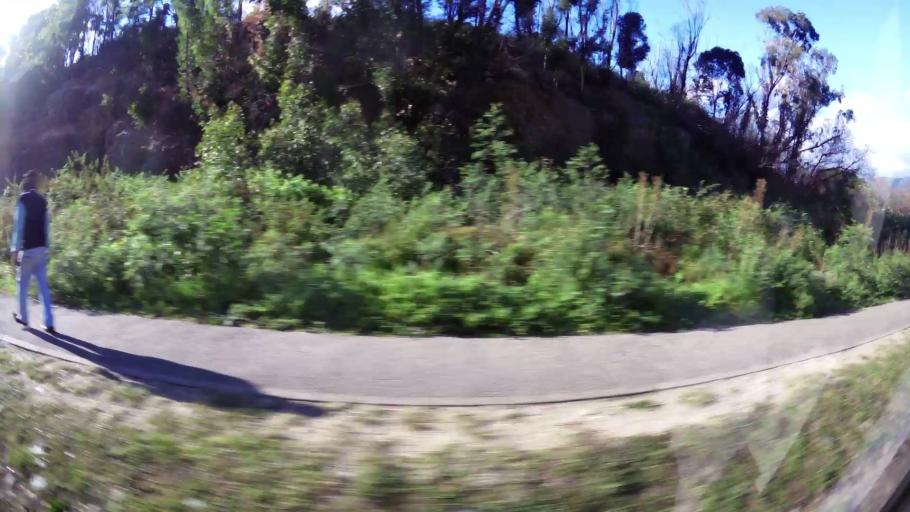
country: ZA
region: Western Cape
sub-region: Eden District Municipality
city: Knysna
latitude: -34.0314
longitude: 23.0472
